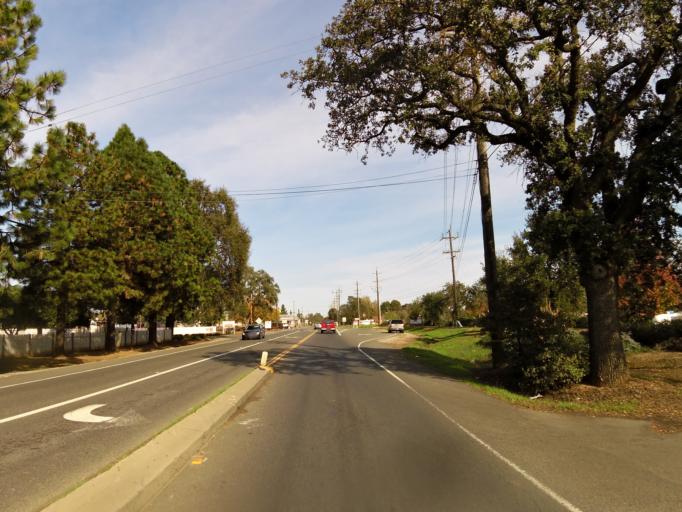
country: US
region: California
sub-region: Sacramento County
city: Wilton
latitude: 38.4312
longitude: -121.3003
